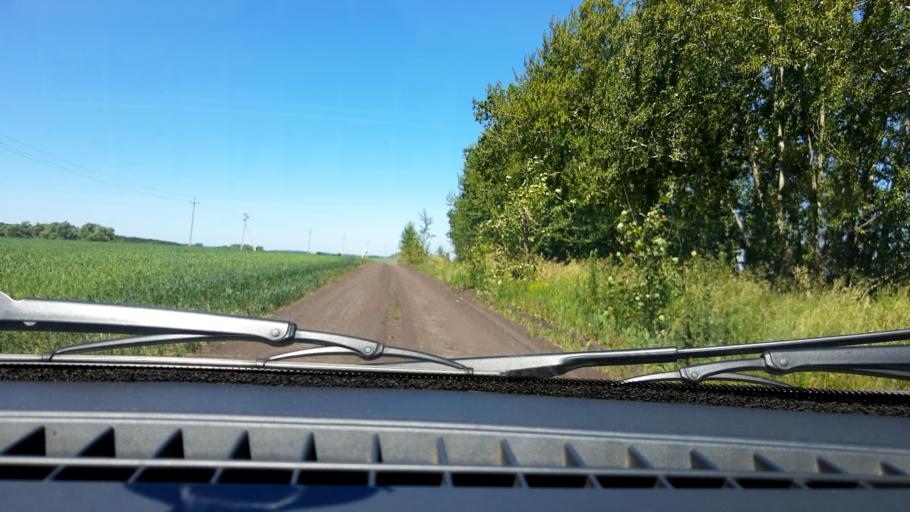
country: RU
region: Bashkortostan
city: Mikhaylovka
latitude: 54.8616
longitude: 55.9353
